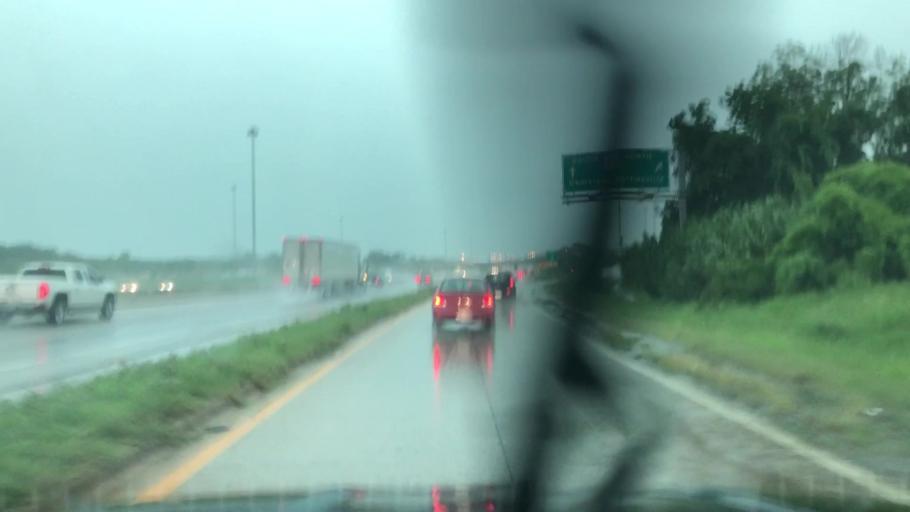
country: US
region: Oklahoma
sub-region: Tulsa County
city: Oakhurst
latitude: 36.0891
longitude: -96.0024
